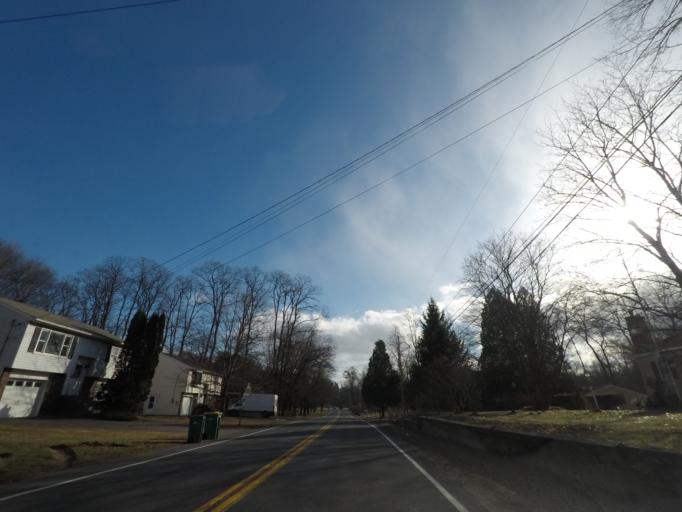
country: US
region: New York
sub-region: Albany County
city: Colonie
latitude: 42.7403
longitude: -73.8688
